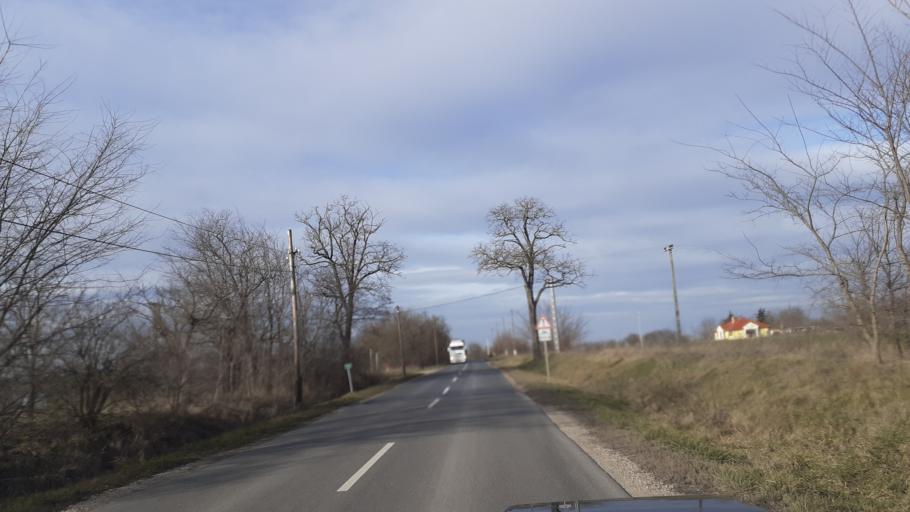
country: HU
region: Fejer
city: Kaloz
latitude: 46.9681
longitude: 18.4829
